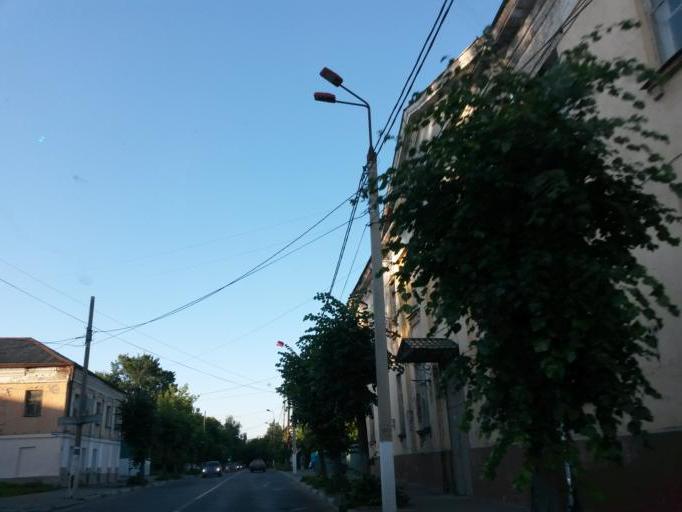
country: RU
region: Moskovskaya
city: Serpukhov
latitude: 54.9188
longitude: 37.4060
